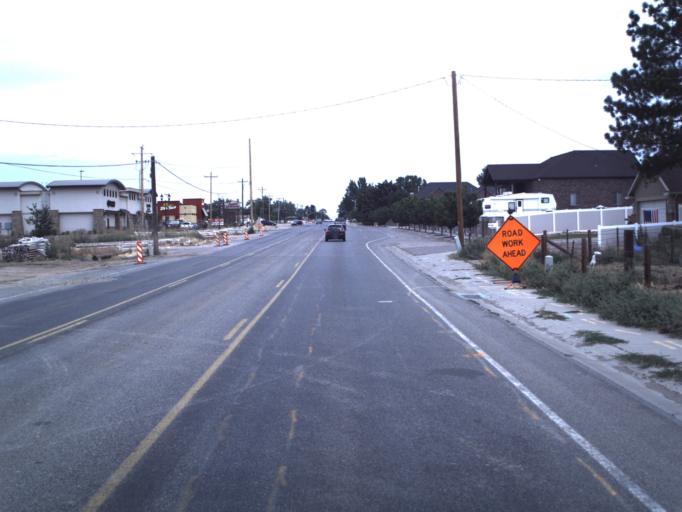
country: US
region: Utah
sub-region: Davis County
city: West Point
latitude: 41.1134
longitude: -112.0645
